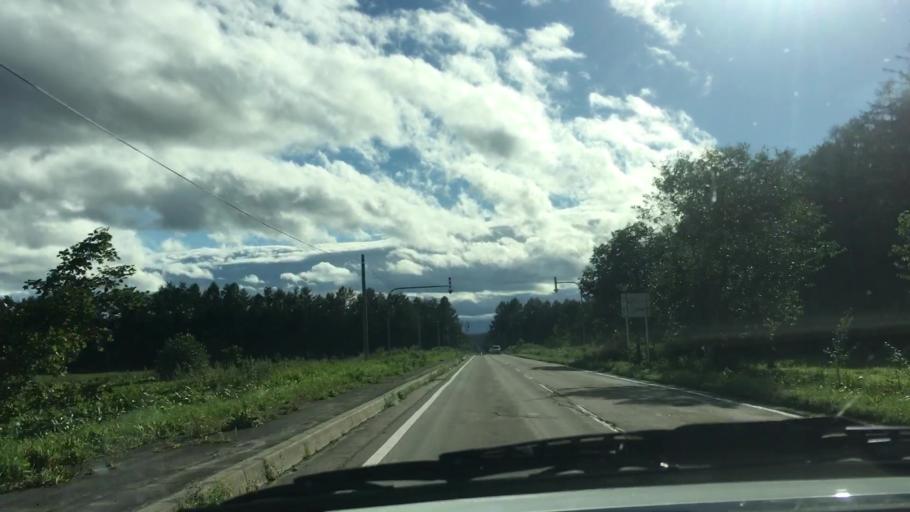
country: JP
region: Hokkaido
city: Otofuke
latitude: 43.1858
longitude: 143.0234
